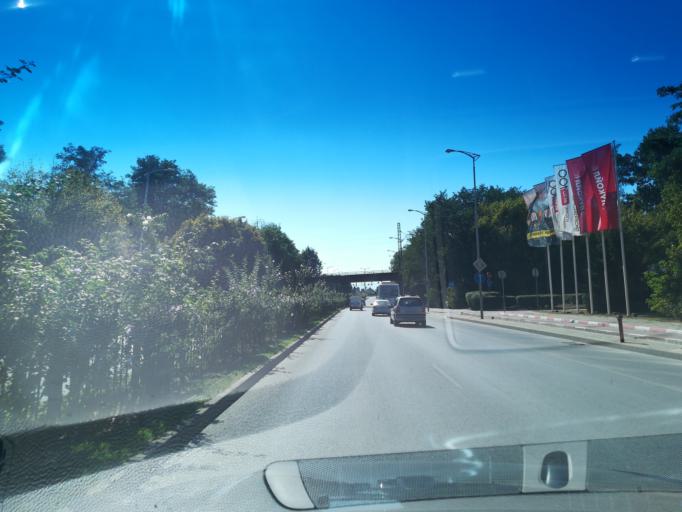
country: BG
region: Plovdiv
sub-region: Obshtina Plovdiv
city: Plovdiv
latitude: 42.1570
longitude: 24.7234
